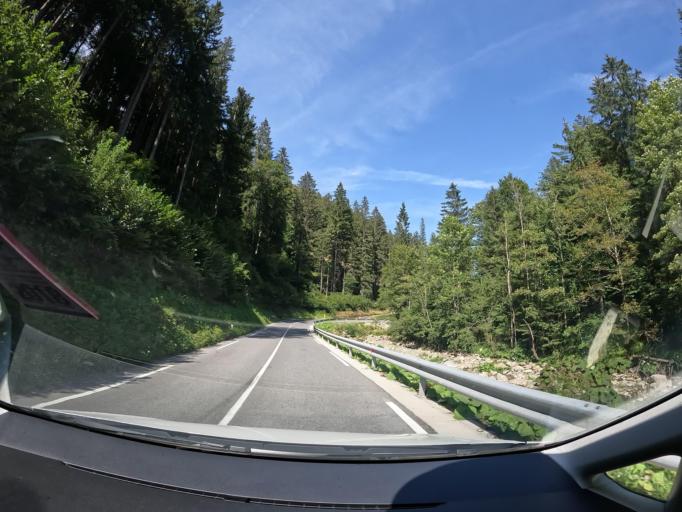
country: SI
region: Zirovnica
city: Zirovnica
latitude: 46.4424
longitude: 14.1716
